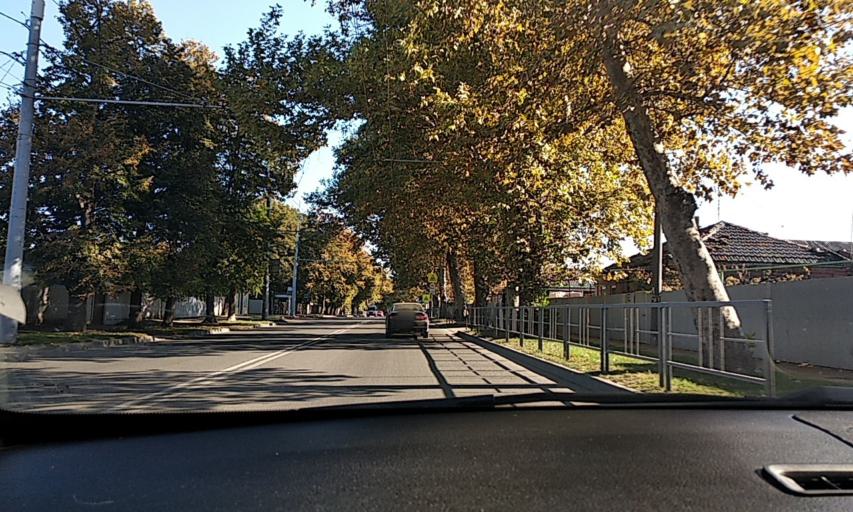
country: RU
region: Krasnodarskiy
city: Pashkovskiy
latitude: 45.0233
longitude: 39.1111
